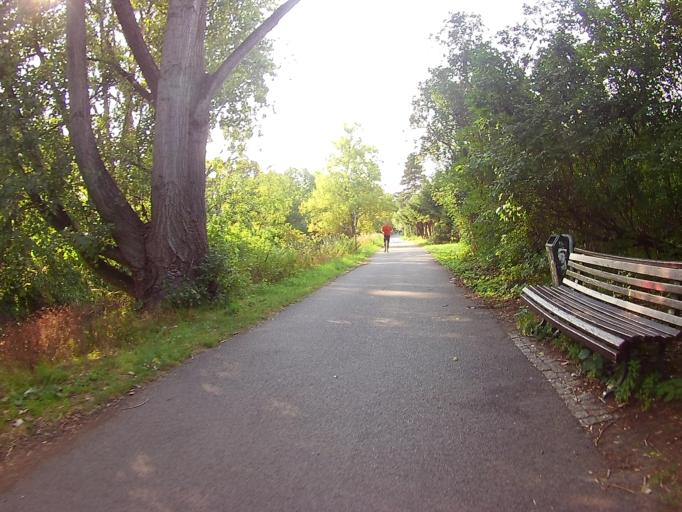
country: DE
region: Berlin
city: Kopenick Bezirk
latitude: 52.4680
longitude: 13.5688
